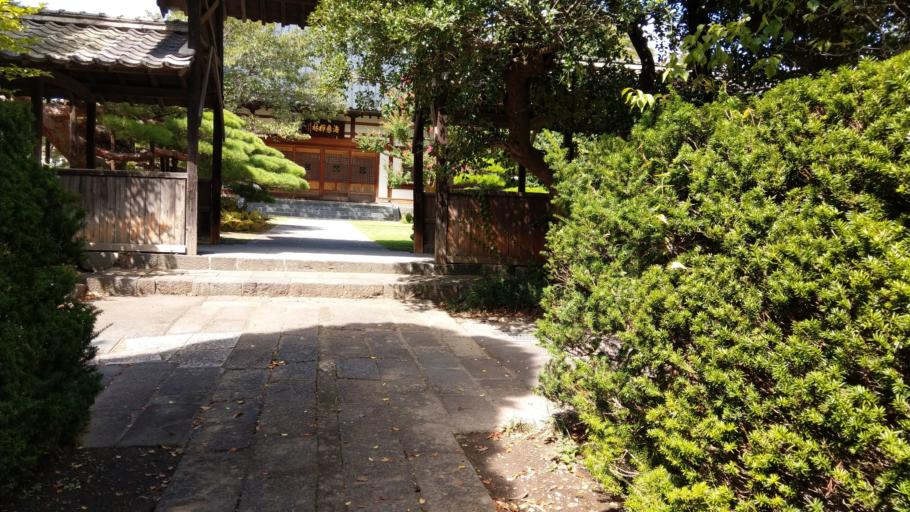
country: JP
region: Nagano
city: Komoro
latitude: 36.3276
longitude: 138.4282
